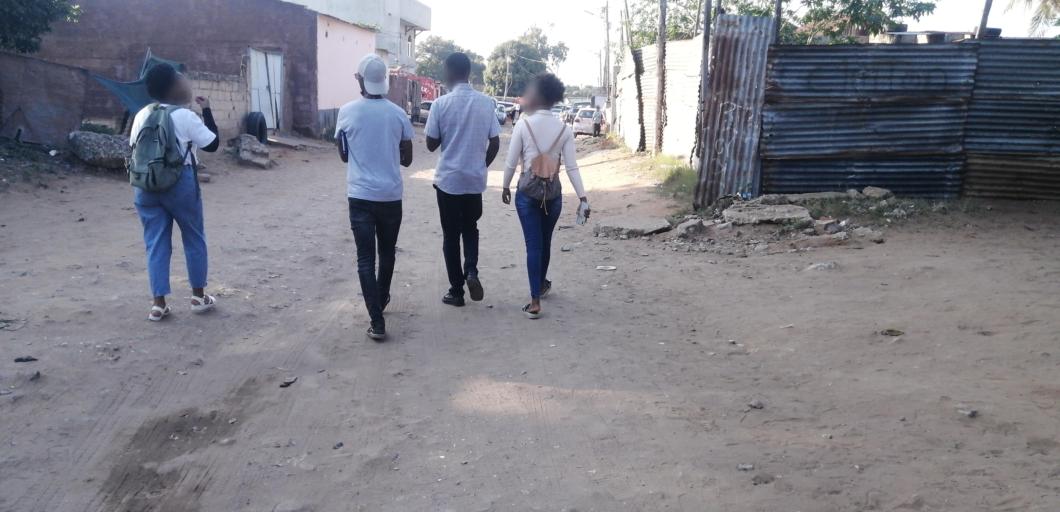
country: MZ
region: Maputo City
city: Maputo
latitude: -25.9551
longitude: 32.5686
